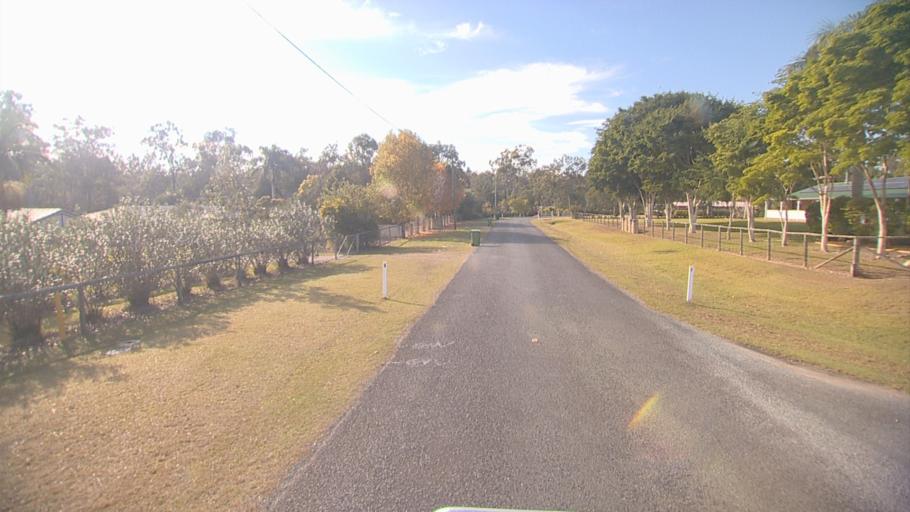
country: AU
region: Queensland
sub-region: Logan
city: Park Ridge South
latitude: -27.7332
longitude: 153.0331
